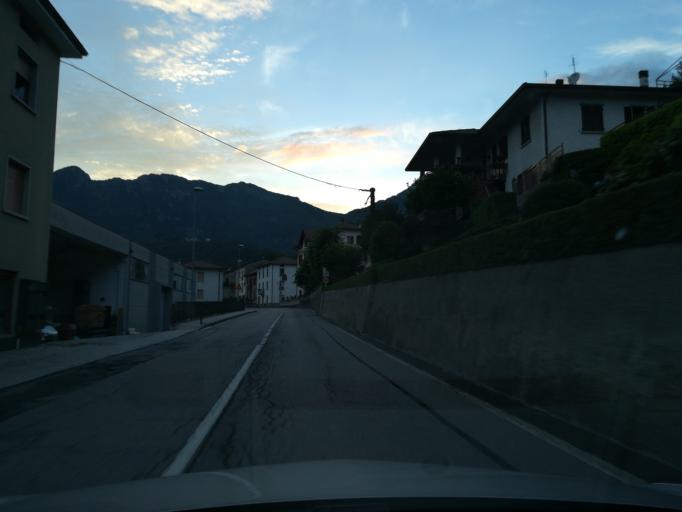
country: IT
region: Lombardy
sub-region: Provincia di Bergamo
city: Rota d'Imagna
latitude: 45.8184
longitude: 9.5215
